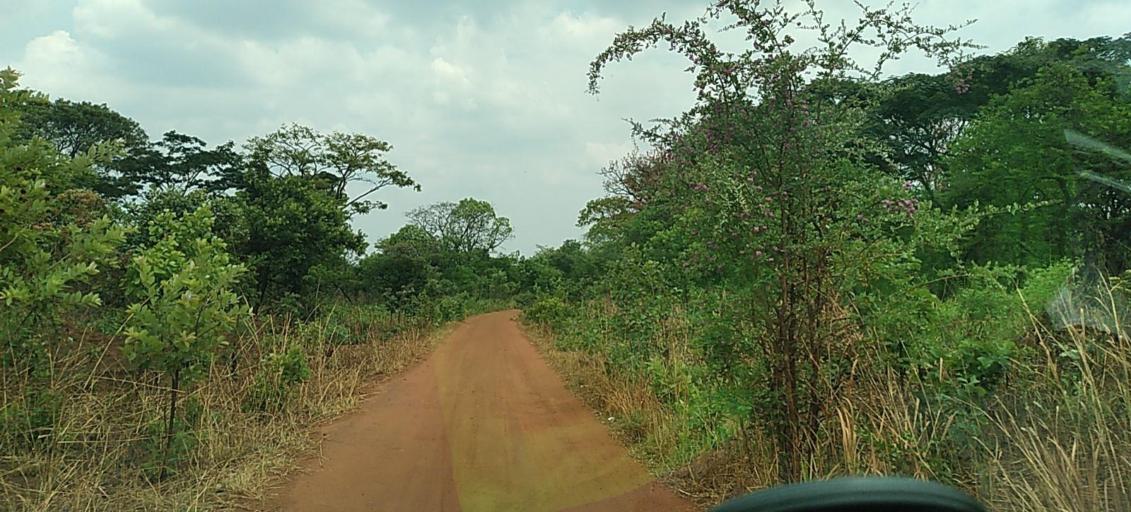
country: ZM
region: North-Western
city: Kansanshi
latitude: -12.0489
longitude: 26.3771
